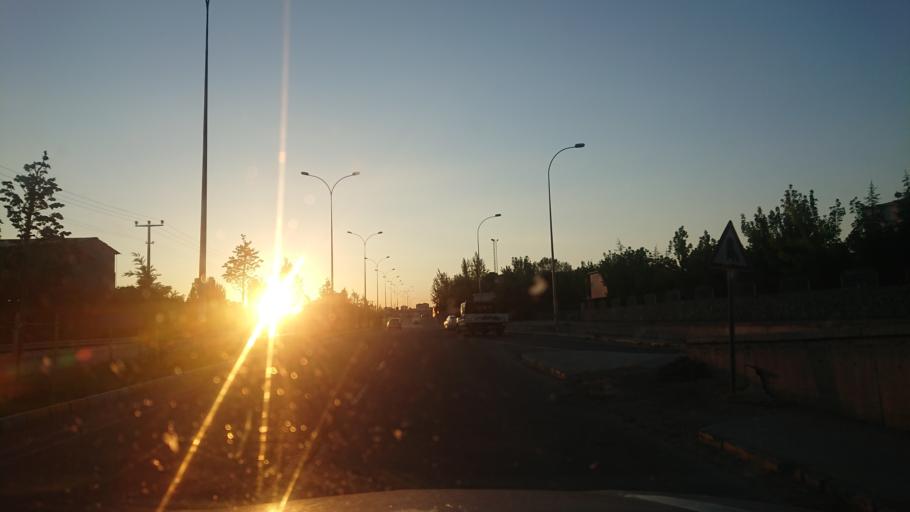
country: TR
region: Aksaray
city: Aksaray
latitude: 38.4014
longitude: 34.0176
